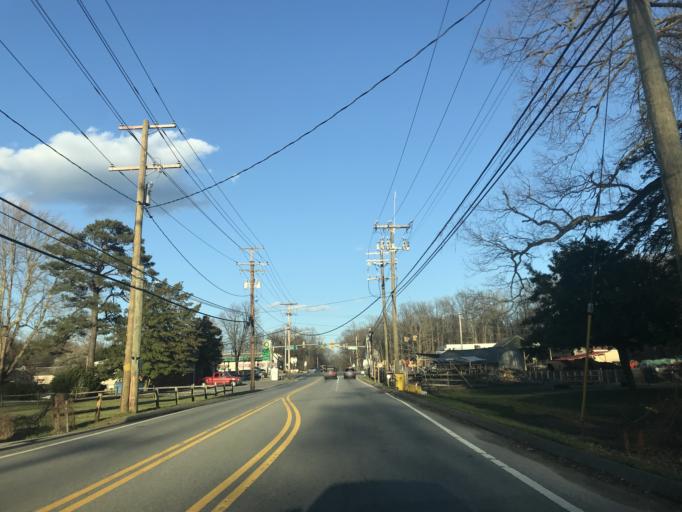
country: US
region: Maryland
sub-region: Anne Arundel County
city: Crofton
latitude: 38.9925
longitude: -76.6721
